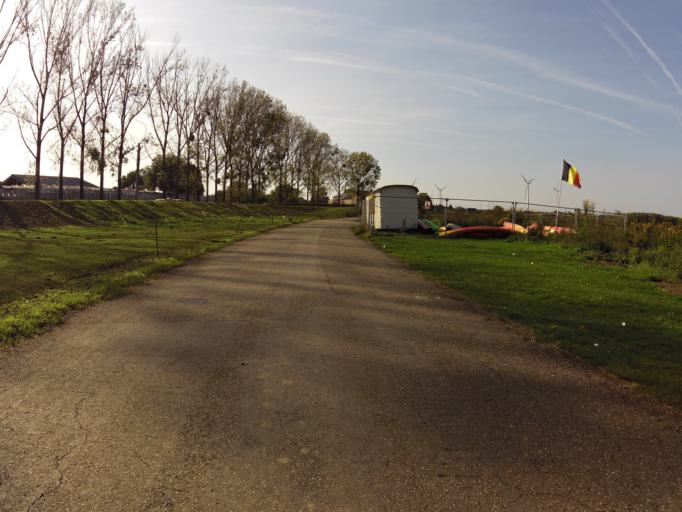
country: NL
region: Limburg
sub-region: Gemeente Stein
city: Stein
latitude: 50.9561
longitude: 5.7378
